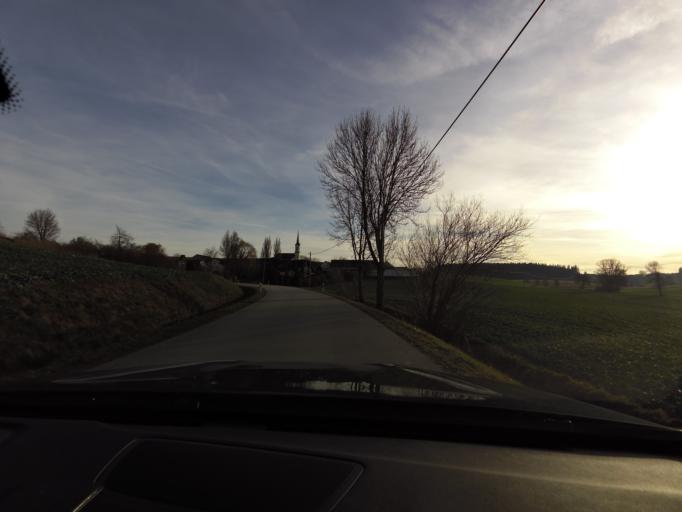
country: DE
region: Bavaria
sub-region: Lower Bavaria
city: Vilsheim
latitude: 48.4305
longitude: 12.1260
